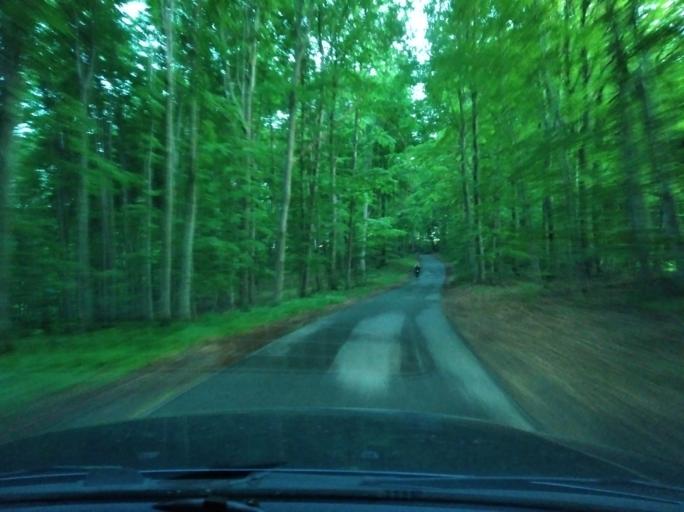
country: PL
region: Subcarpathian Voivodeship
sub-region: Powiat strzyzowski
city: Czudec
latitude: 49.9230
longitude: 21.8387
